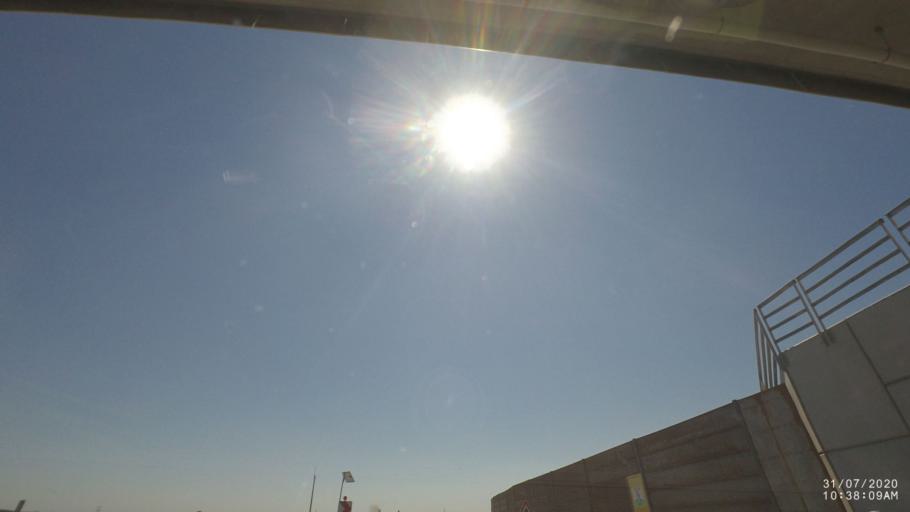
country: SK
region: Trnavsky
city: Dunajska Streda
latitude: 48.0042
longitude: 17.4860
